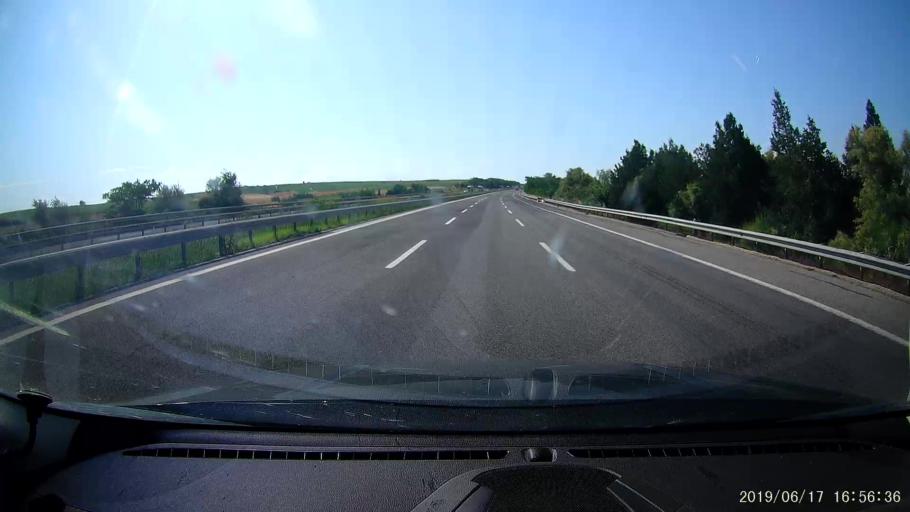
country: TR
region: Edirne
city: Haskoy
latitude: 41.5885
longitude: 26.9326
